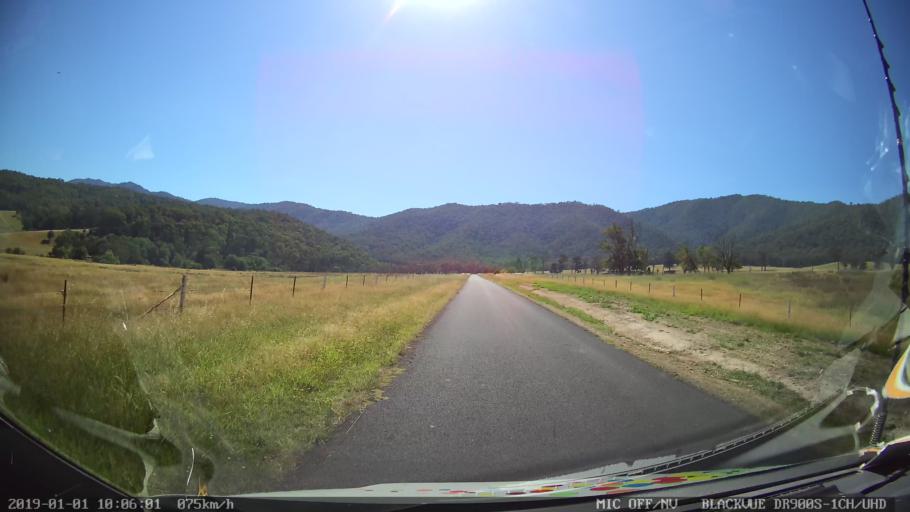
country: AU
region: New South Wales
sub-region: Snowy River
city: Jindabyne
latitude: -36.1747
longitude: 148.1429
